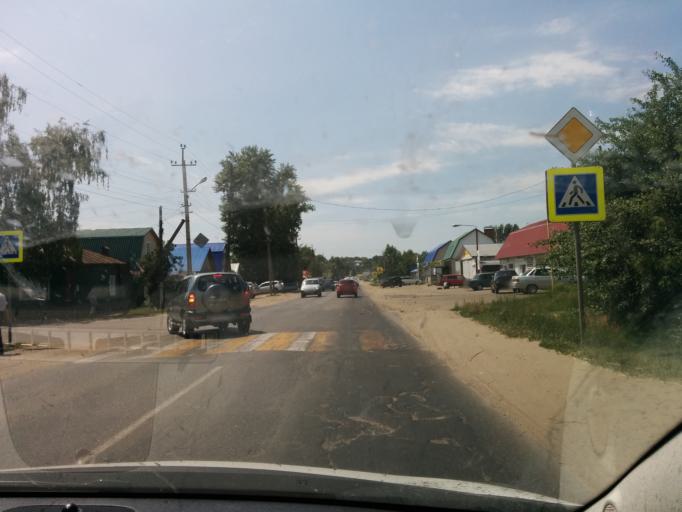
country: RU
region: Tambov
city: Morshansk
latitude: 53.4463
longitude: 41.8068
